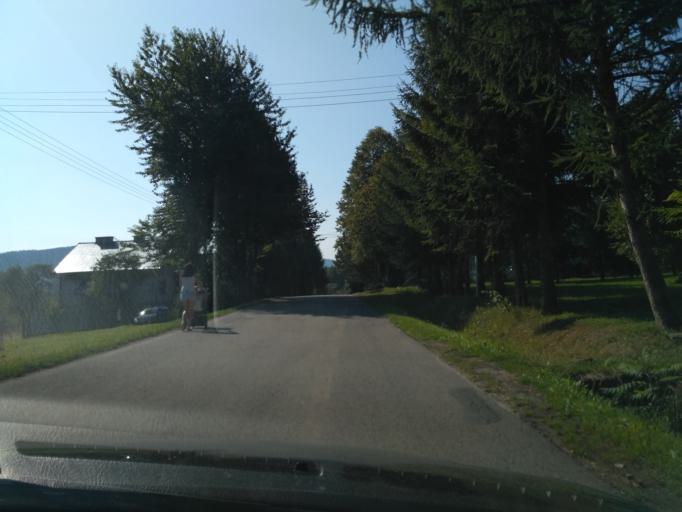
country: PL
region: Subcarpathian Voivodeship
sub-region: Powiat strzyzowski
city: Wysoka Strzyzowska
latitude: 49.8096
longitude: 21.7448
